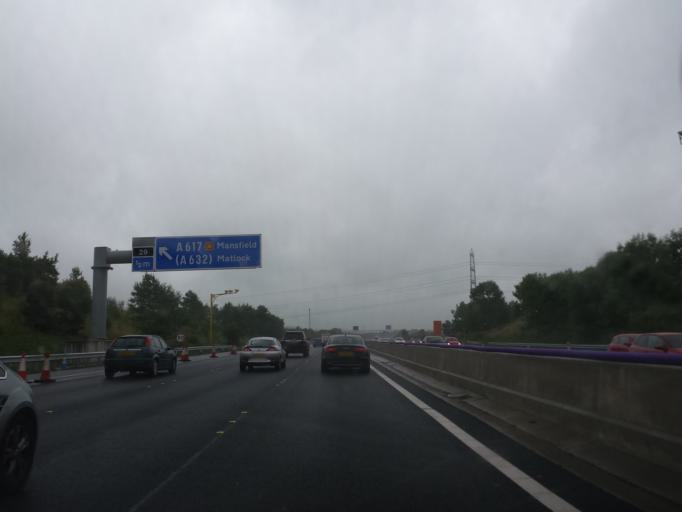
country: GB
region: England
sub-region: Derbyshire
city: Bolsover
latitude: 53.2125
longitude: -1.3235
